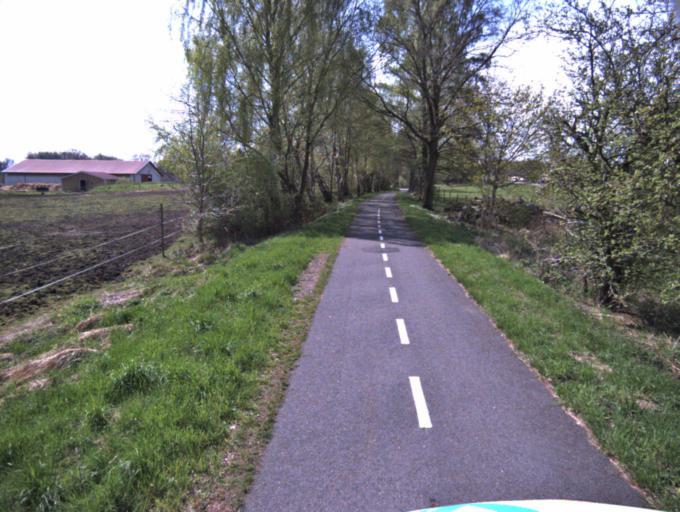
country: SE
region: Skane
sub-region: Kristianstads Kommun
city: Onnestad
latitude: 56.0005
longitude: 14.0440
